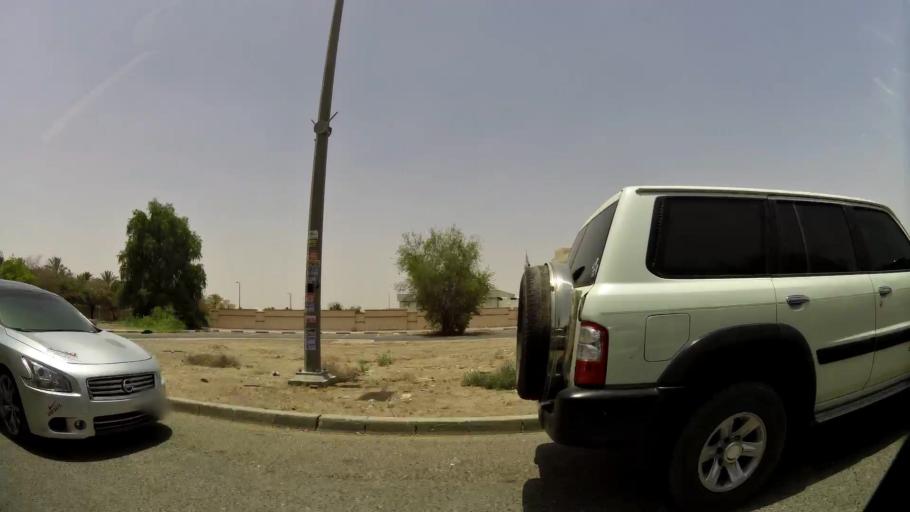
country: AE
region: Abu Dhabi
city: Al Ain
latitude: 24.2174
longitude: 55.7143
